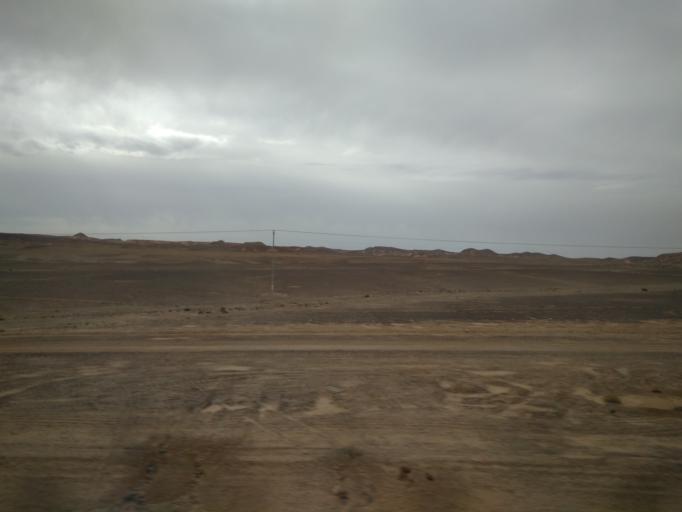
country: IL
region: Southern District
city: Eilat
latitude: 29.8839
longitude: 34.8531
